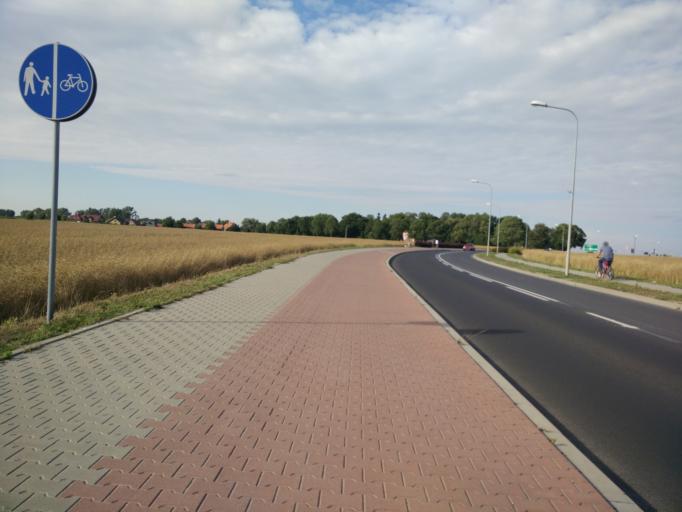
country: PL
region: Greater Poland Voivodeship
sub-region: Powiat sredzki
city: Sroda Wielkopolska
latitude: 52.2375
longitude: 17.2715
